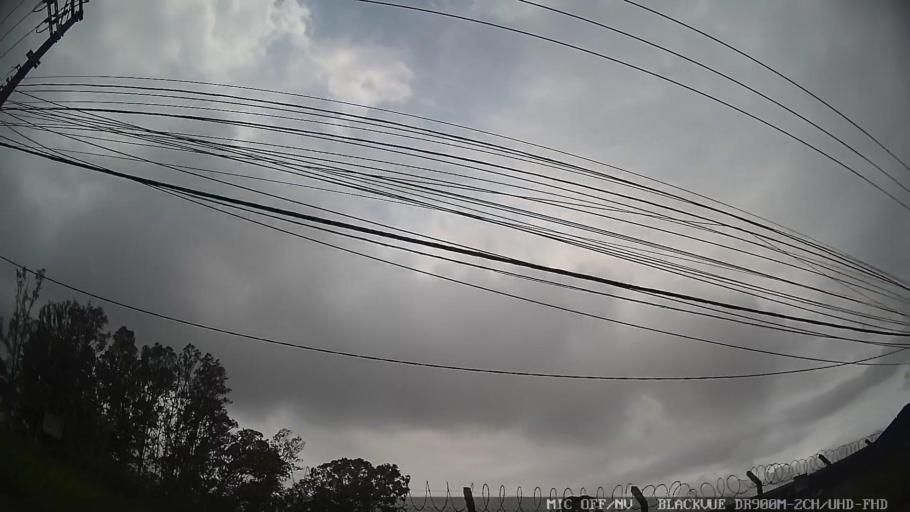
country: BR
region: Sao Paulo
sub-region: Osasco
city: Osasco
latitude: -23.4826
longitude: -46.7815
